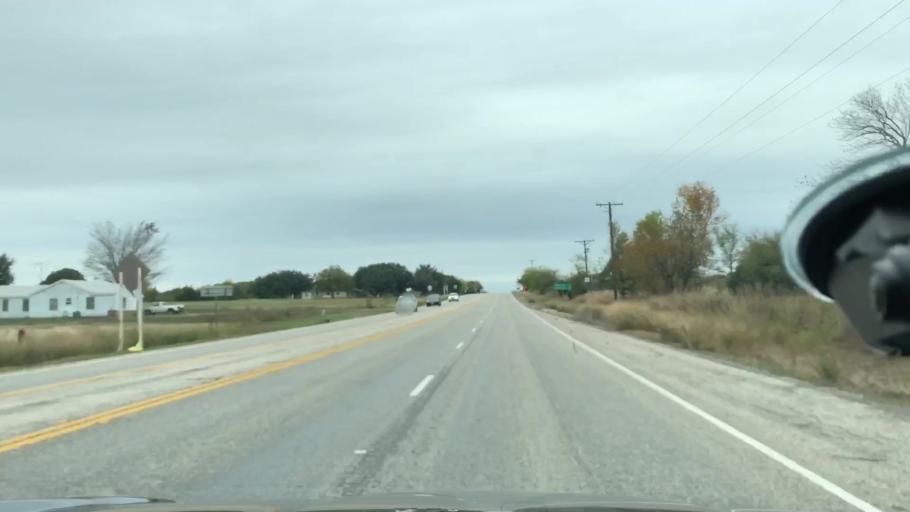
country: US
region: Texas
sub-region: Hunt County
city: Quinlan
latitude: 32.9491
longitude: -96.1075
